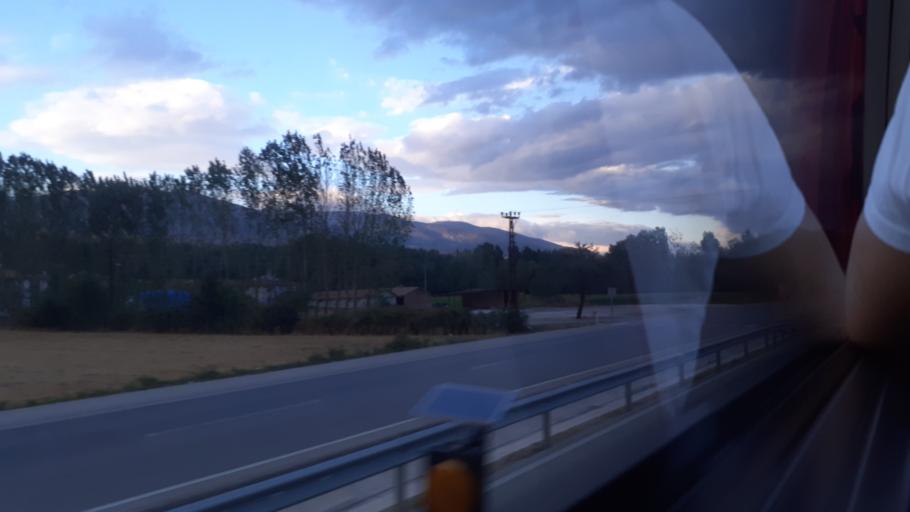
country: TR
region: Tokat
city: Dokmetepe
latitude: 40.3222
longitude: 36.2228
